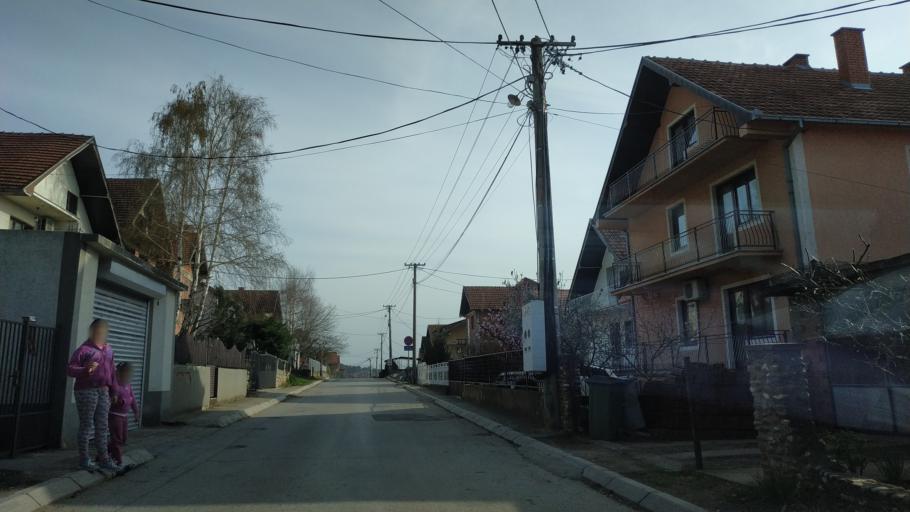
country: RS
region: Central Serbia
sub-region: Nisavski Okrug
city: Aleksinac
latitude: 43.5460
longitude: 21.7172
